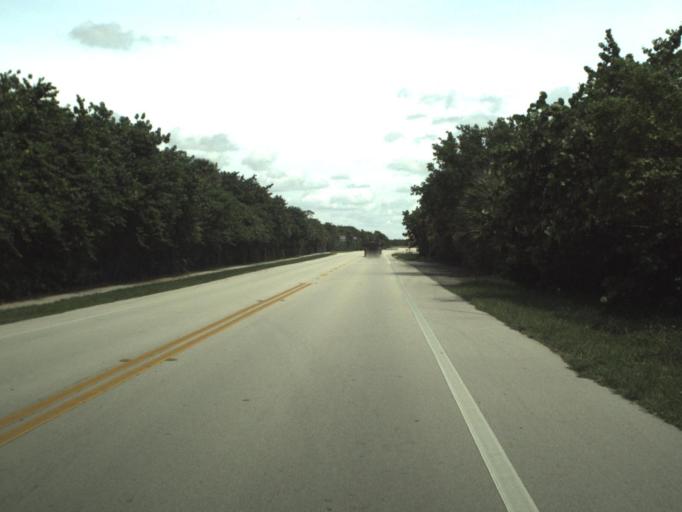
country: US
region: Florida
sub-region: Palm Beach County
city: Lake Park
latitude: 26.8144
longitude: -80.0372
